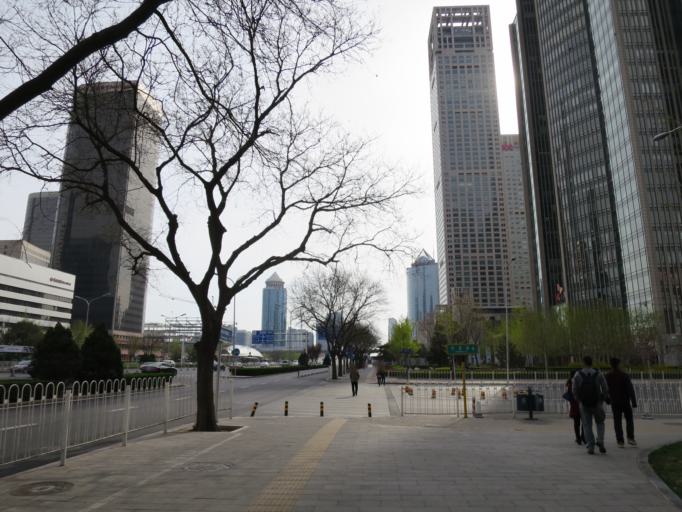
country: CN
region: Beijing
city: Chaowai
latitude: 39.9068
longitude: 116.4492
